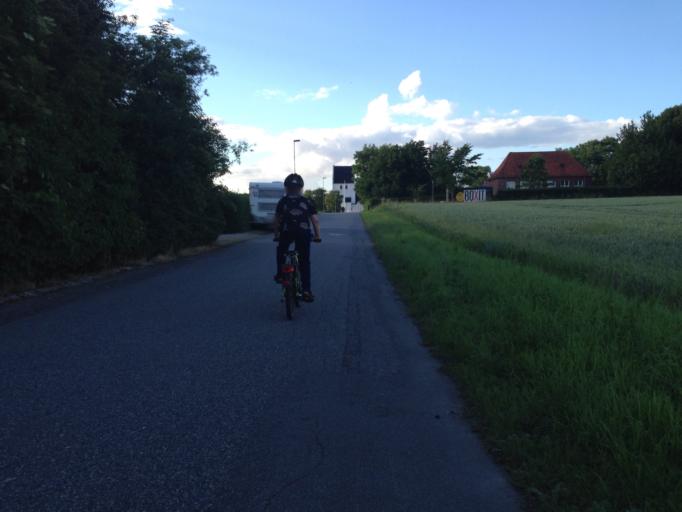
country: DK
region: South Denmark
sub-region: Middelfart Kommune
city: Norre Aby
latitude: 55.4817
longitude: 9.9035
